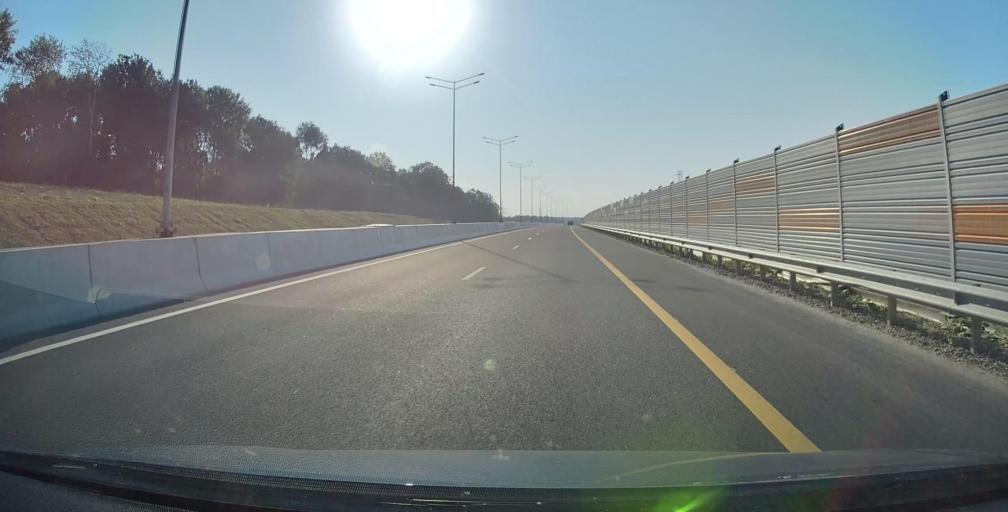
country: RU
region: Moskovskaya
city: Yel'digino
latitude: 56.1310
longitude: 37.8664
